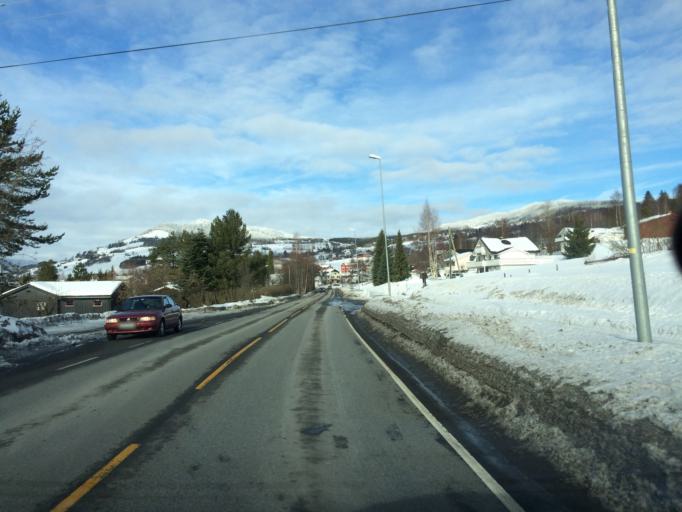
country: NO
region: Oppland
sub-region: Gausdal
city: Segalstad bru
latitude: 61.2110
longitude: 10.2953
